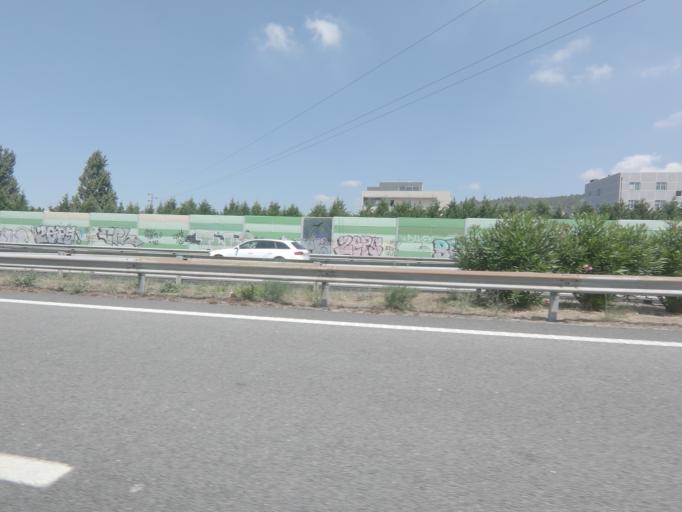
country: PT
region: Porto
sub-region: Valongo
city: Valongo
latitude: 41.1967
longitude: -8.4943
